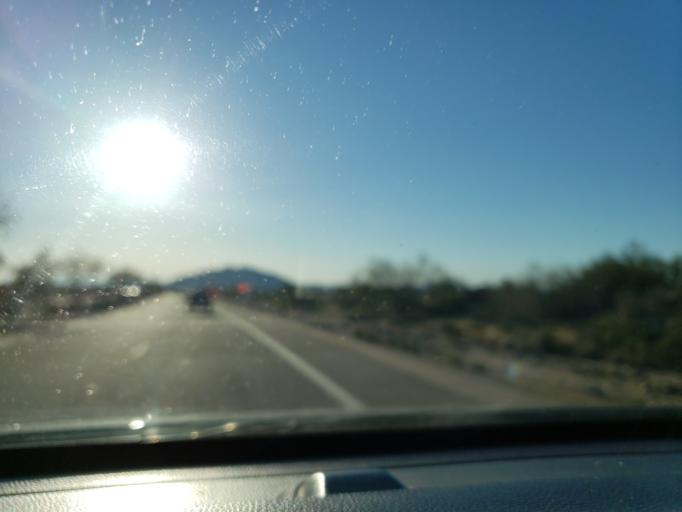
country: US
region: Arizona
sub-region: Maricopa County
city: Carefree
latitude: 33.8261
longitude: -111.8684
